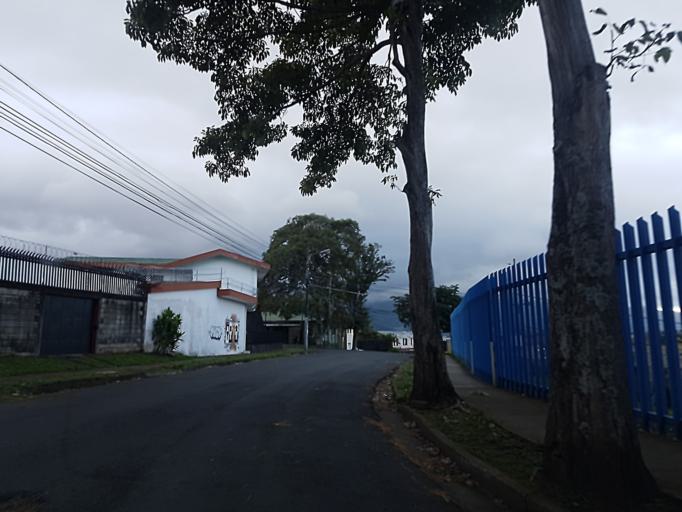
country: CR
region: San Jose
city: San Pedro
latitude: 9.9279
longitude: -84.0501
